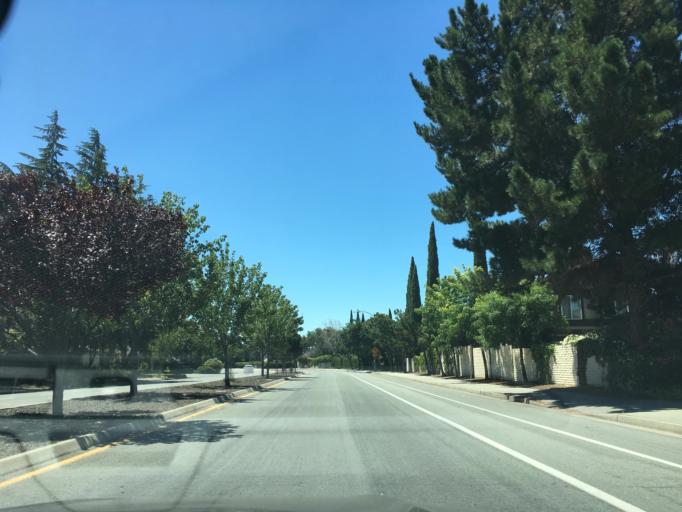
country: US
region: California
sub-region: Santa Clara County
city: East Foothills
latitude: 37.3881
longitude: -121.8430
